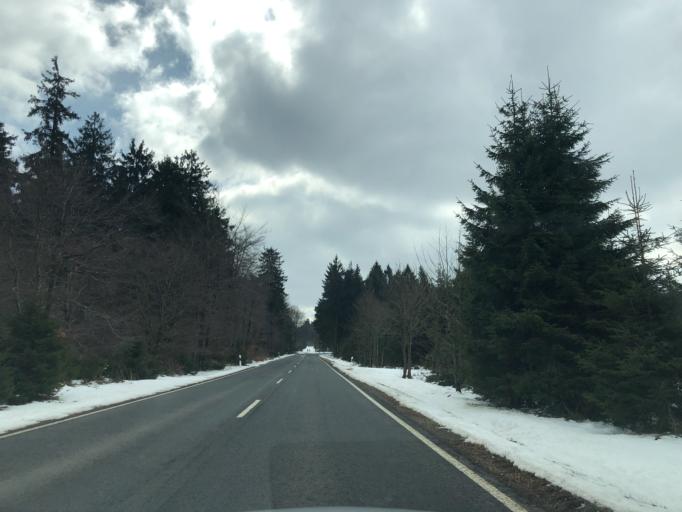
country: DE
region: Hesse
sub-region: Regierungsbezirk Giessen
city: Ulrichstein
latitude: 50.5258
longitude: 9.2354
